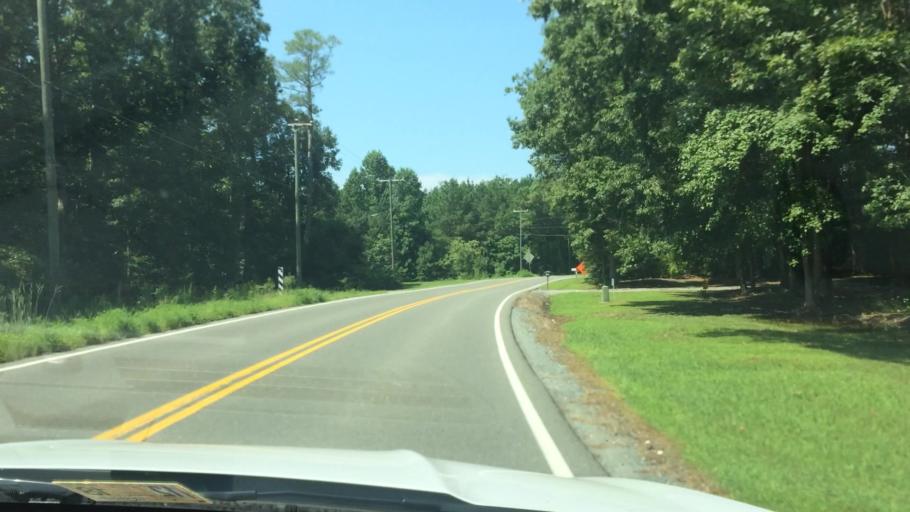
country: US
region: Virginia
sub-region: New Kent County
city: New Kent
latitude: 37.5320
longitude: -77.1091
